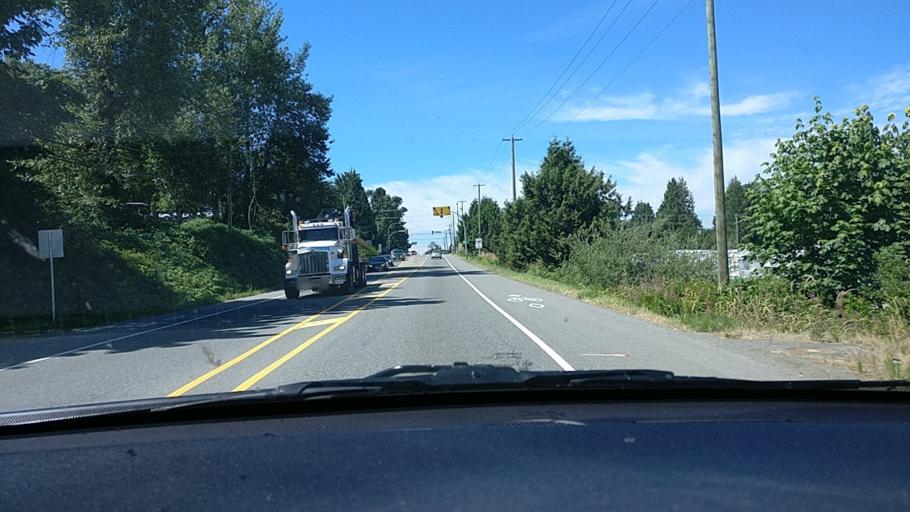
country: CA
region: British Columbia
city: Aldergrove
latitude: 49.0571
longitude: -122.4231
